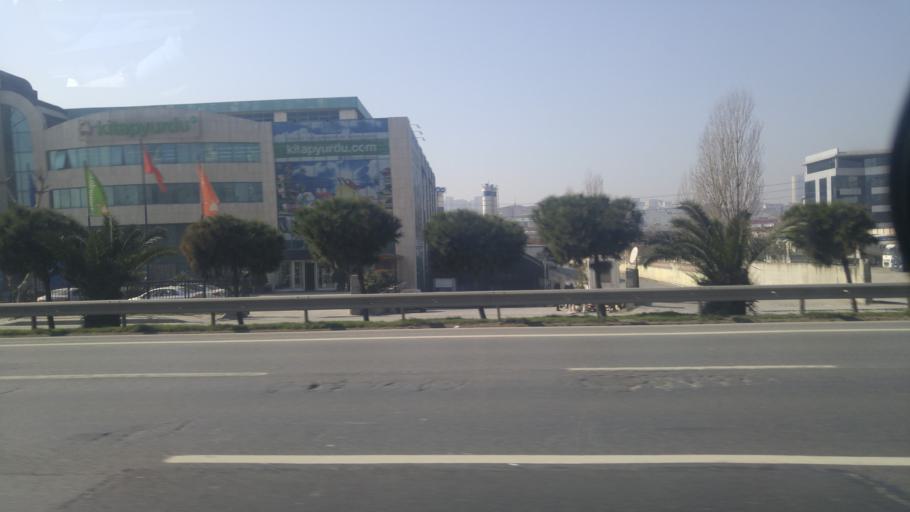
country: TR
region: Istanbul
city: Mahmutbey
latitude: 41.0238
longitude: 28.8114
